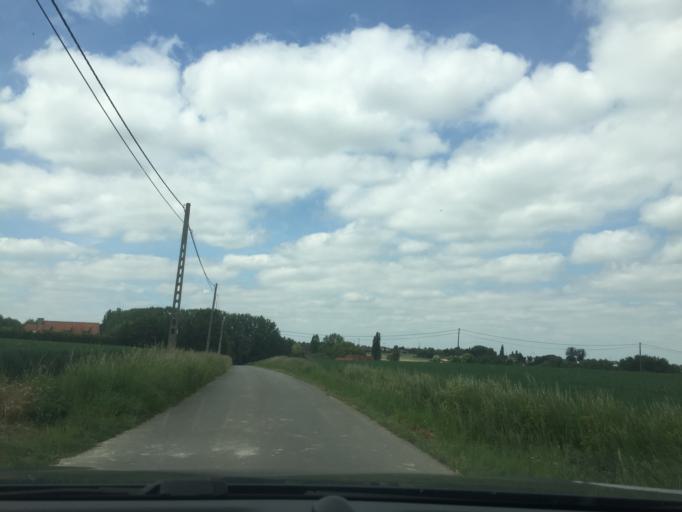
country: BE
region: Flanders
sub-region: Provincie West-Vlaanderen
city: Zwevegem
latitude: 50.7833
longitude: 3.3278
